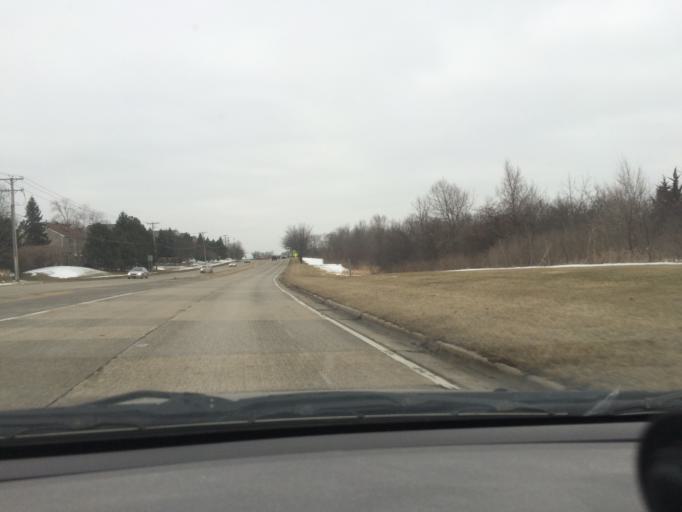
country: US
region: Illinois
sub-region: Cook County
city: Streamwood
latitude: 42.0360
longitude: -88.1792
